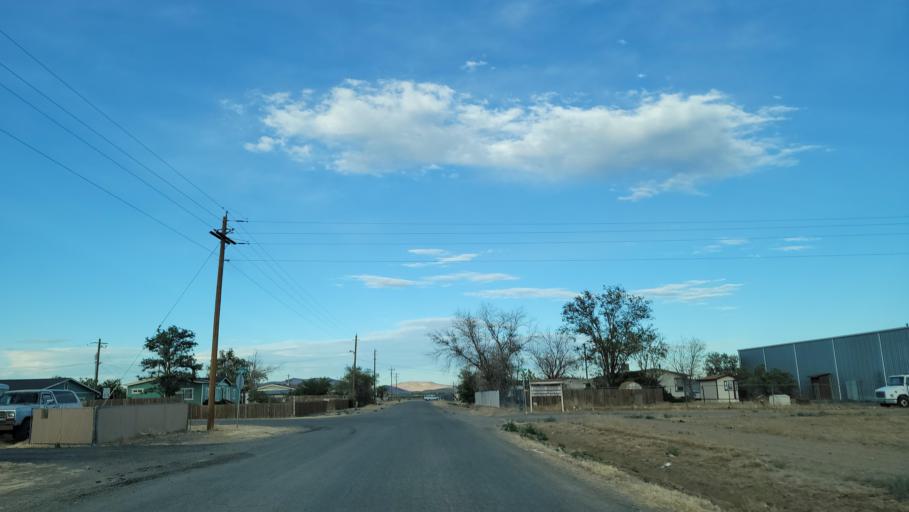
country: US
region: Nevada
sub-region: Lyon County
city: Silver Springs
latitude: 39.4044
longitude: -119.2182
